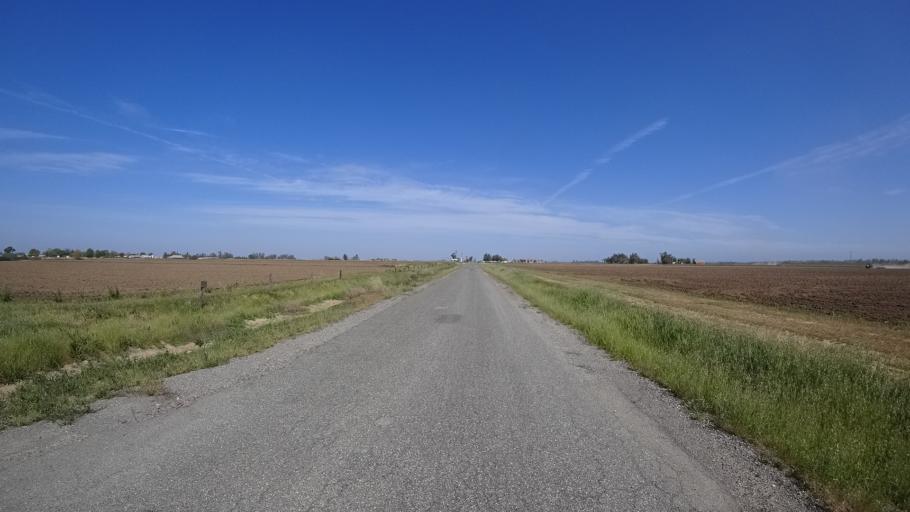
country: US
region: California
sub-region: Glenn County
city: Hamilton City
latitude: 39.5730
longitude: -122.0280
